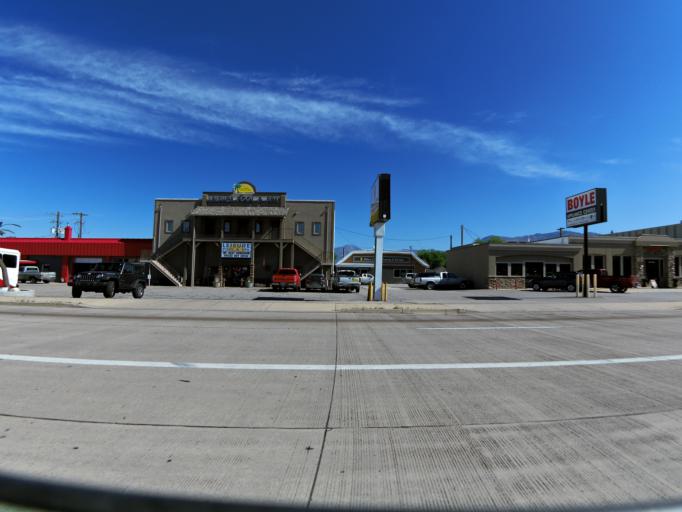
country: US
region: Utah
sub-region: Weber County
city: South Ogden
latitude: 41.1978
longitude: -111.9785
